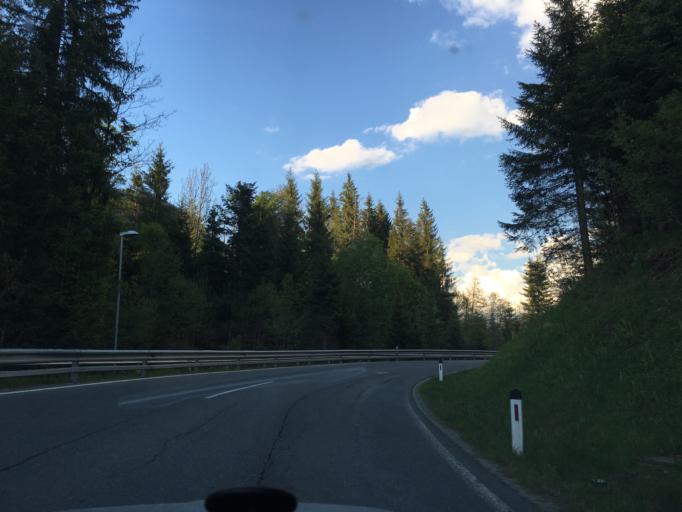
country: AT
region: Tyrol
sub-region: Politischer Bezirk Kitzbuhel
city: Fieberbrunn
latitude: 47.4961
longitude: 12.5443
